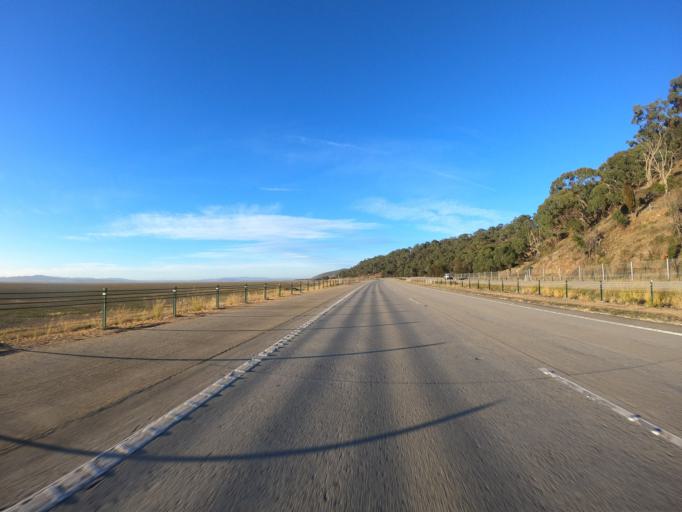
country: AU
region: New South Wales
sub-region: Yass Valley
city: Gundaroo
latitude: -35.0851
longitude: 149.3745
